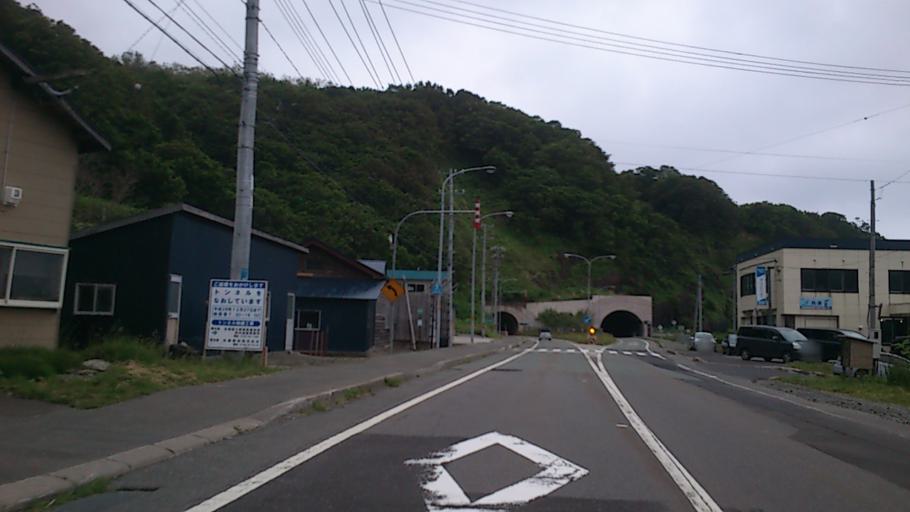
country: JP
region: Hokkaido
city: Iwanai
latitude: 42.7400
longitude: 140.1129
